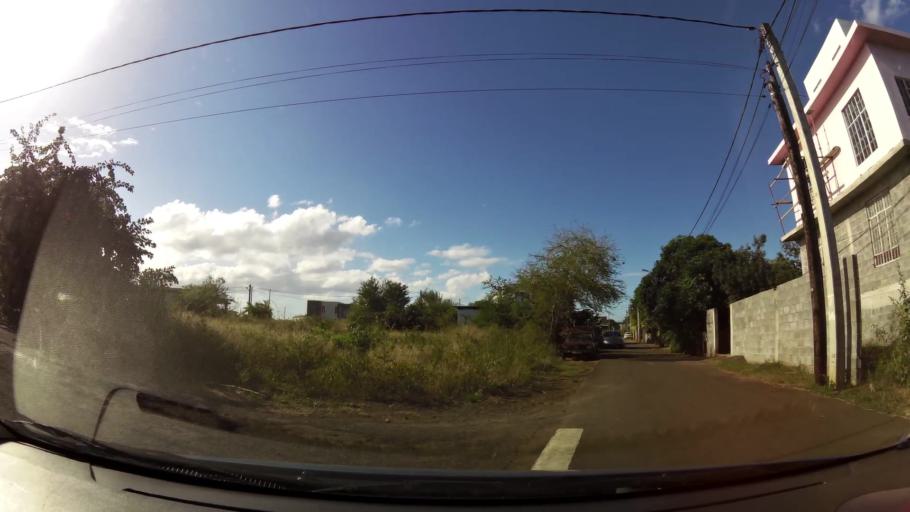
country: MU
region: Black River
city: Gros Cailloux
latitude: -20.2050
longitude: 57.4158
